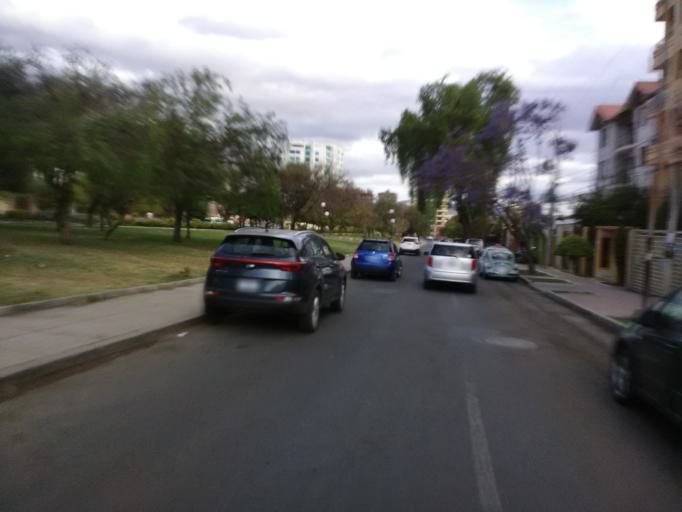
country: BO
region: Cochabamba
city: Cochabamba
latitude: -17.3699
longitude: -66.1592
